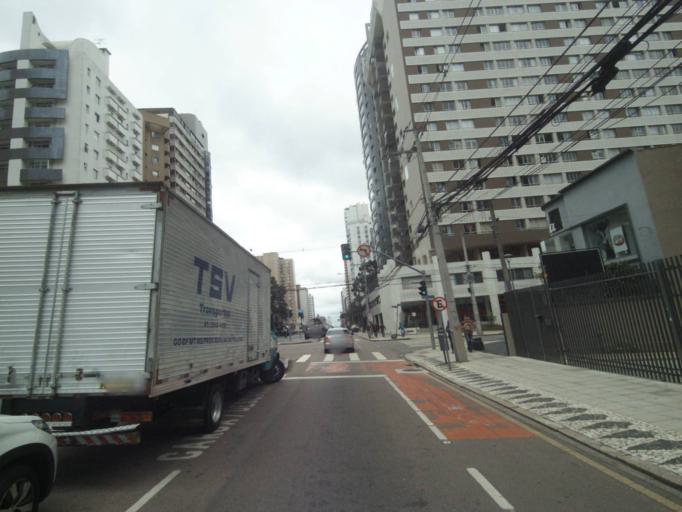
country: BR
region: Parana
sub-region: Curitiba
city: Curitiba
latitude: -25.4439
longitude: -49.2827
